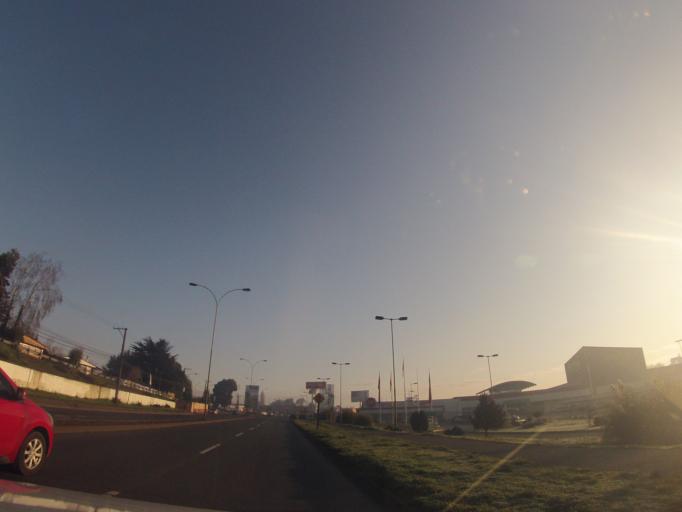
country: CL
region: Araucania
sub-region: Provincia de Cautin
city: Temuco
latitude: -38.7472
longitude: -72.6090
